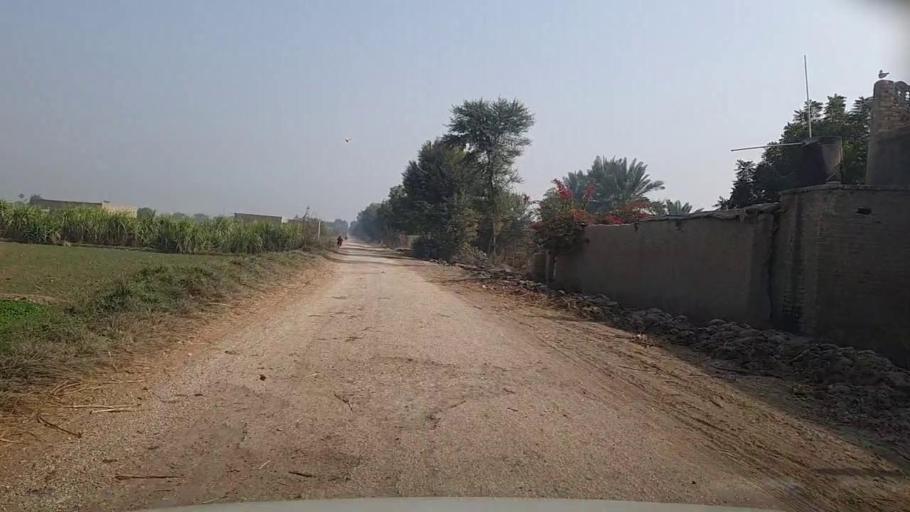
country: PK
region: Sindh
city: Setharja Old
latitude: 27.1305
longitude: 68.5137
